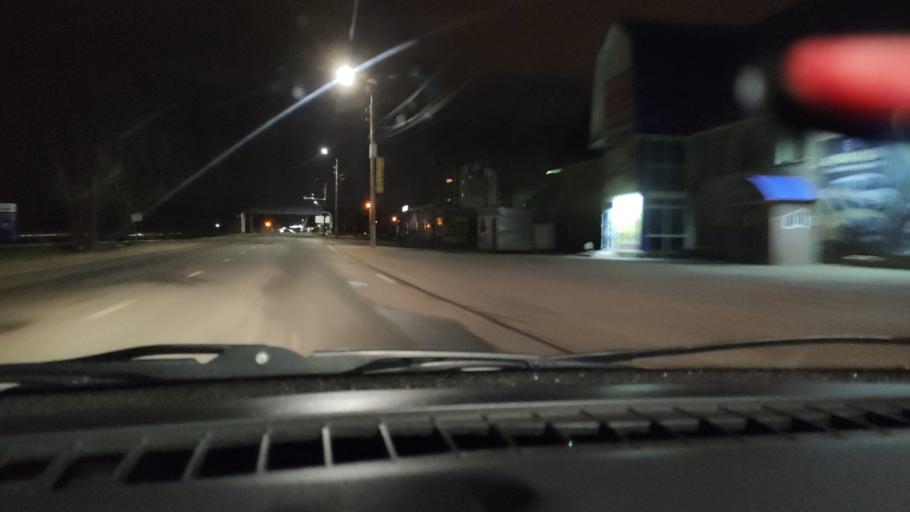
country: RU
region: Bashkortostan
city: Sterlitamak
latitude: 53.6425
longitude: 55.8960
